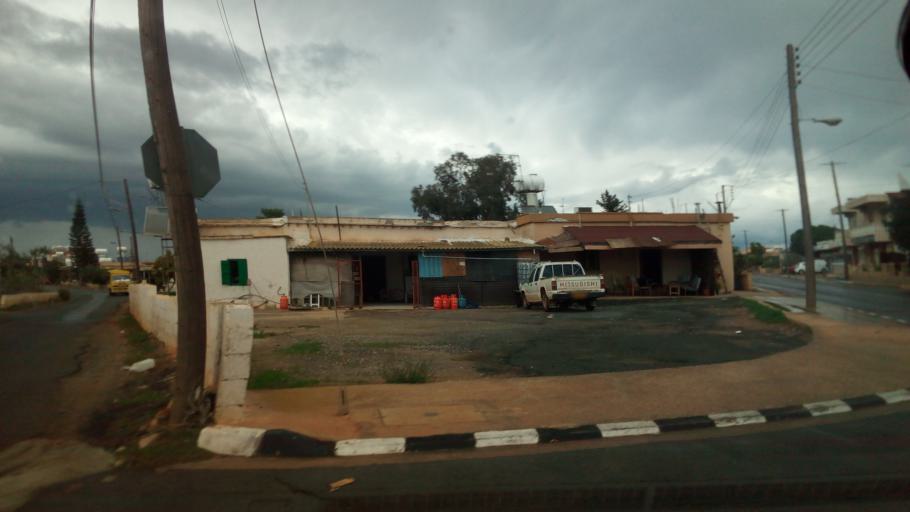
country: CY
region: Ammochostos
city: Liopetri
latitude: 35.0105
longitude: 33.8934
